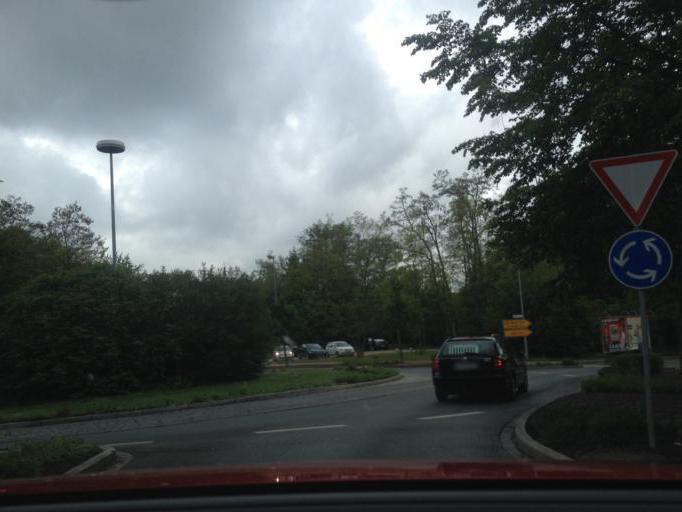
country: DE
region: Bavaria
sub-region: Regierungsbezirk Mittelfranken
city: Rothenbach an der Pegnitz
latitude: 49.4803
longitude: 11.2403
